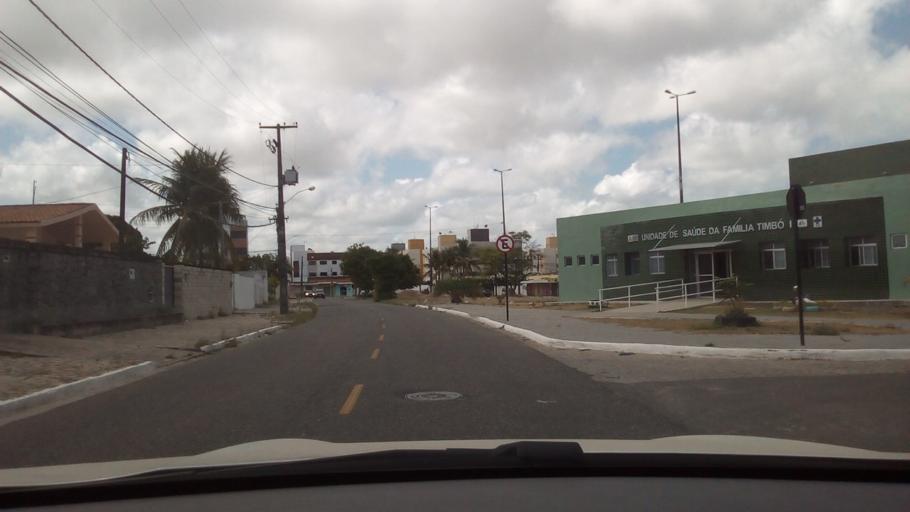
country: BR
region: Paraiba
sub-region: Joao Pessoa
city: Joao Pessoa
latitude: -7.1455
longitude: -34.8342
